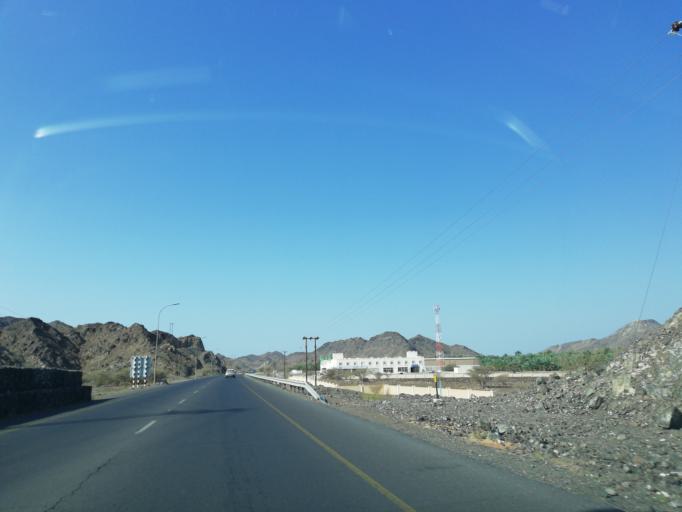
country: OM
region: Ash Sharqiyah
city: Ibra'
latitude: 22.8294
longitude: 58.1705
